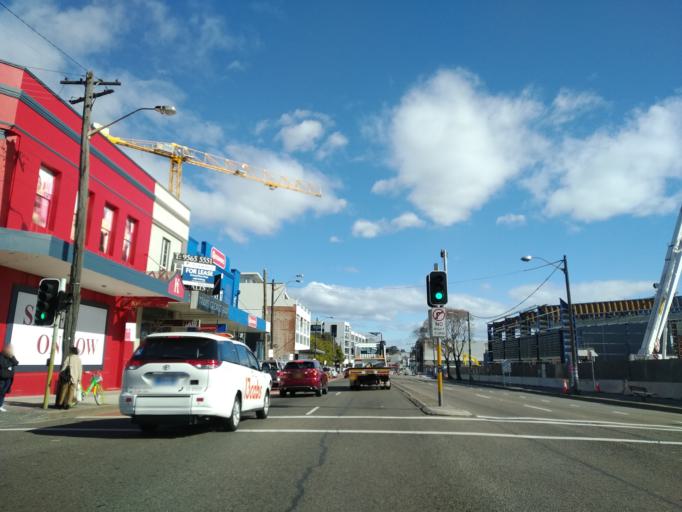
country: AU
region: New South Wales
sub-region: Marrickville
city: Camperdown
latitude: -33.8868
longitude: 151.1766
